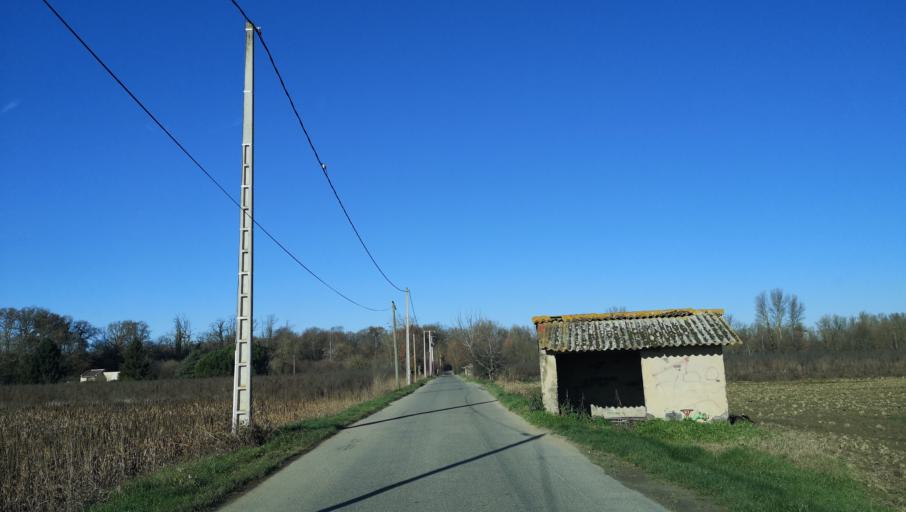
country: FR
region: Midi-Pyrenees
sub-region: Departement de la Haute-Garonne
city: Beauzelle
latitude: 43.6585
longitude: 1.3956
